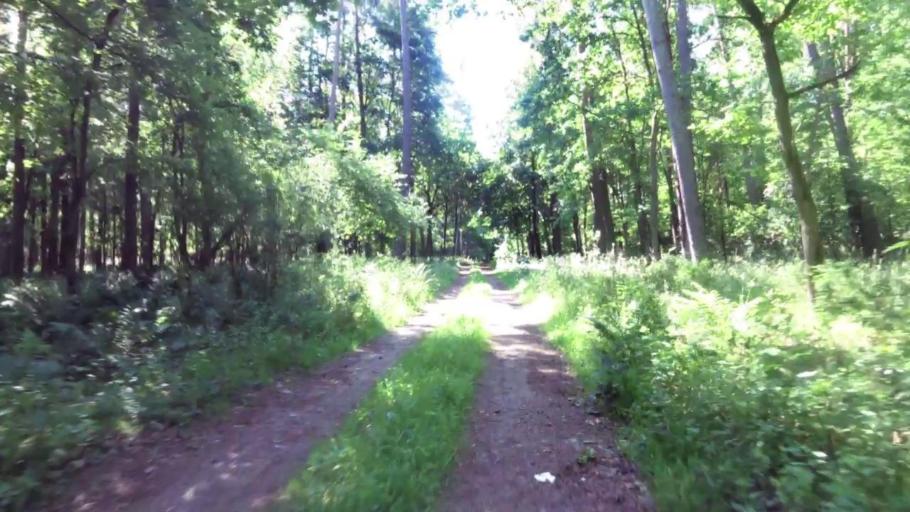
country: PL
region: West Pomeranian Voivodeship
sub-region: Powiat swidwinski
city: Polczyn-Zdroj
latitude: 53.8810
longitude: 16.0960
